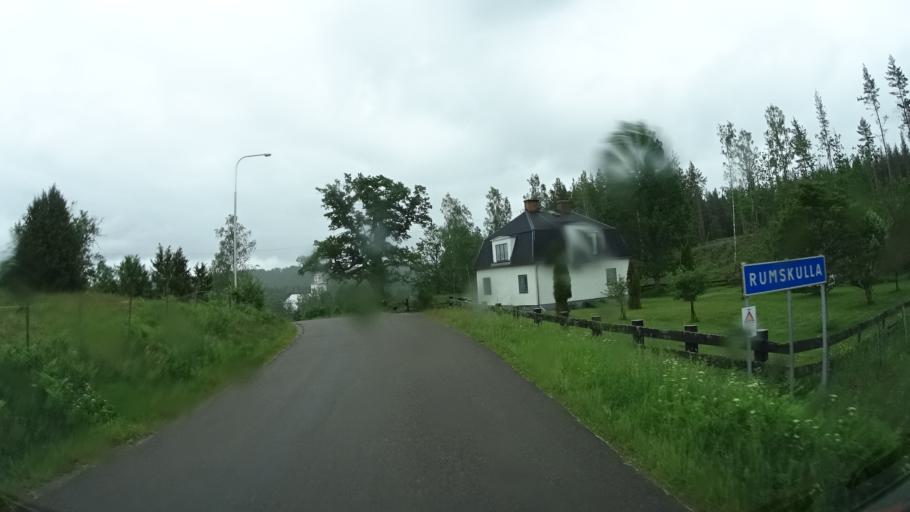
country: SE
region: Joenkoeping
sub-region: Eksjo Kommun
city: Mariannelund
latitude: 57.6772
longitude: 15.5848
